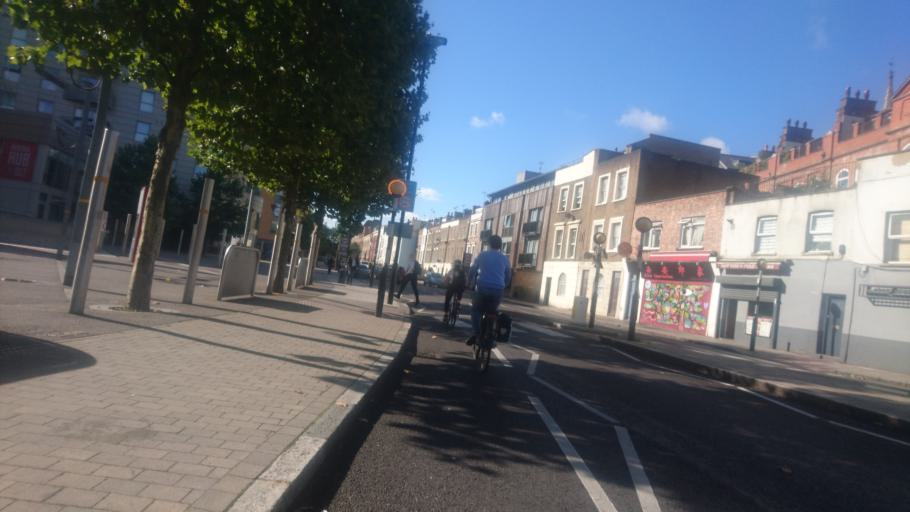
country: GB
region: England
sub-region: Greater London
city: Holloway
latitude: 51.5541
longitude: -0.1103
